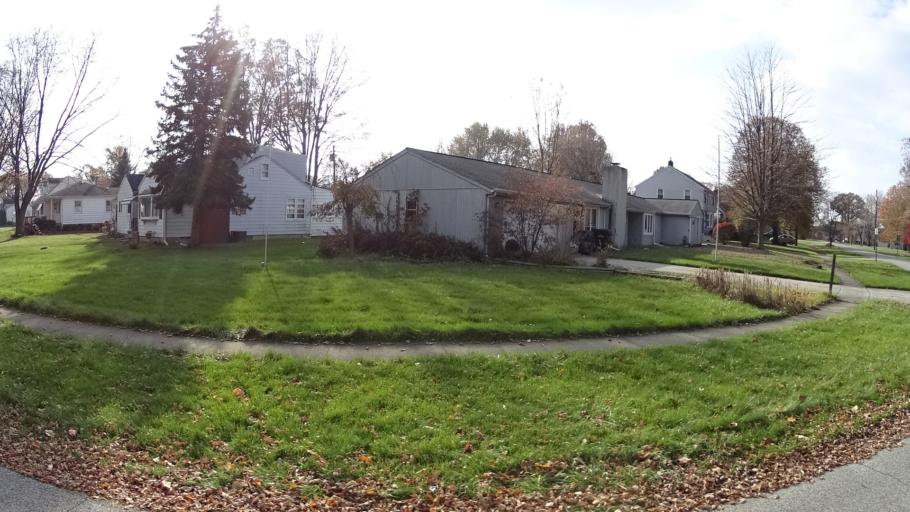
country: US
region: Ohio
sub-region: Lorain County
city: Elyria
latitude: 41.3896
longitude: -82.0891
